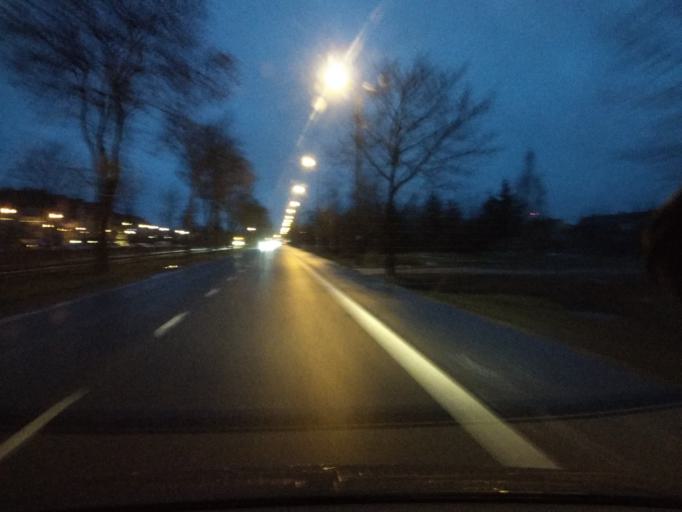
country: PL
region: Lower Silesian Voivodeship
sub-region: Powiat wroclawski
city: Smolec
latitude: 51.1433
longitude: 16.8947
